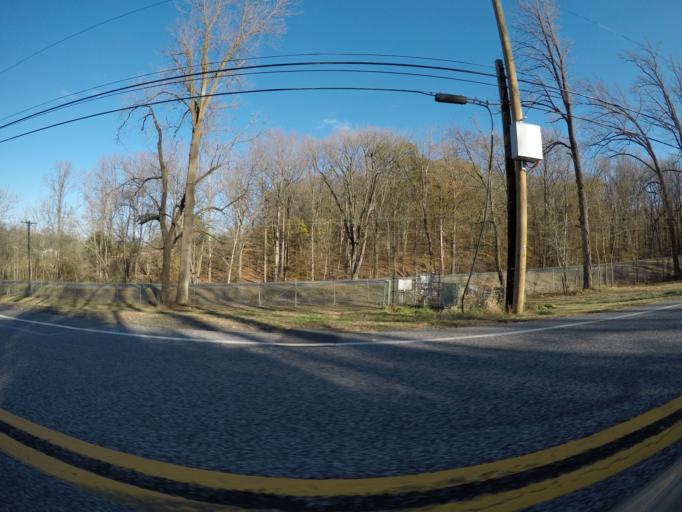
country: US
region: Maryland
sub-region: Harford County
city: South Bel Air
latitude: 39.5962
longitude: -76.2594
